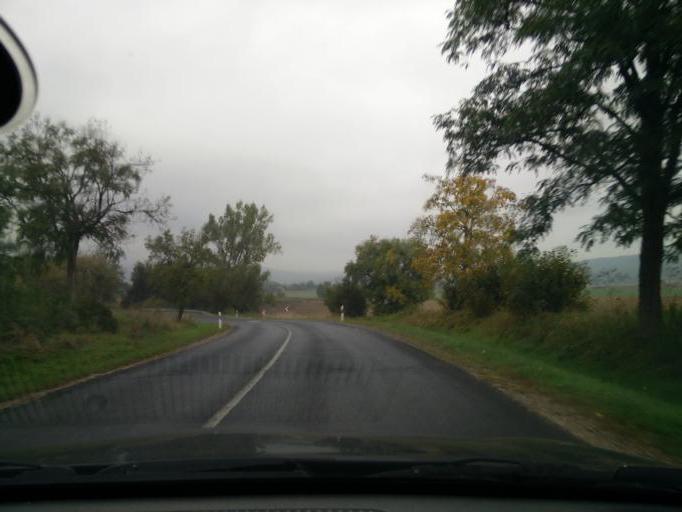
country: HU
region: Komarom-Esztergom
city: Tarjan
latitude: 47.6323
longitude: 18.5171
